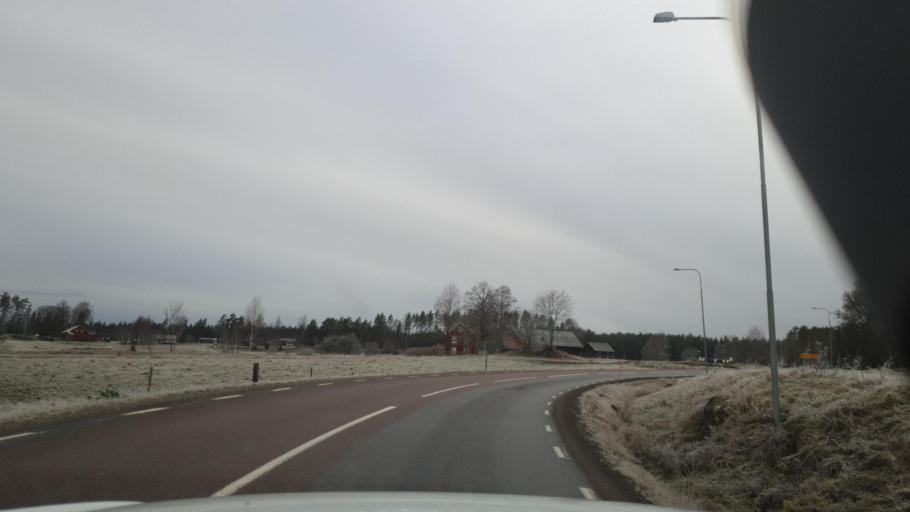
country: SE
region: Vaermland
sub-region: Sunne Kommun
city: Sunne
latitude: 59.6637
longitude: 13.0048
